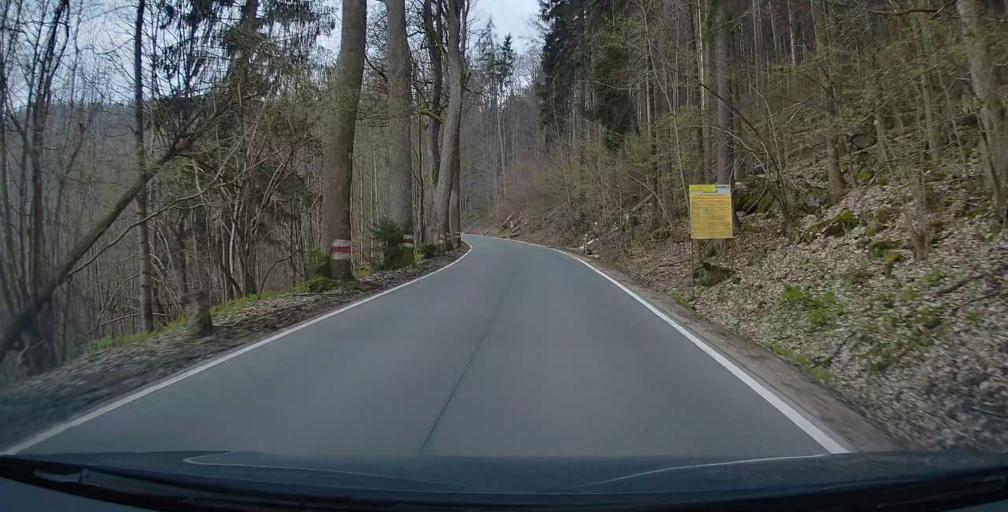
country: PL
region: Lower Silesian Voivodeship
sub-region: Powiat klodzki
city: Radkow
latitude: 50.4878
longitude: 16.3730
